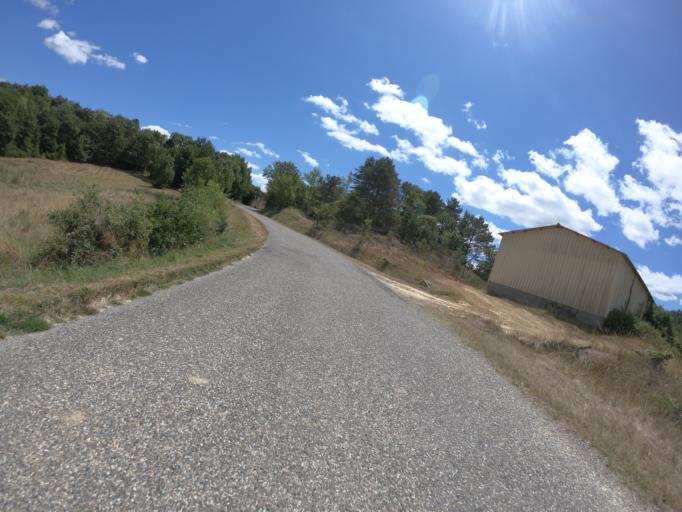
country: FR
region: Midi-Pyrenees
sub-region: Departement de l'Ariege
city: Mirepoix
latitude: 43.0528
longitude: 1.8355
